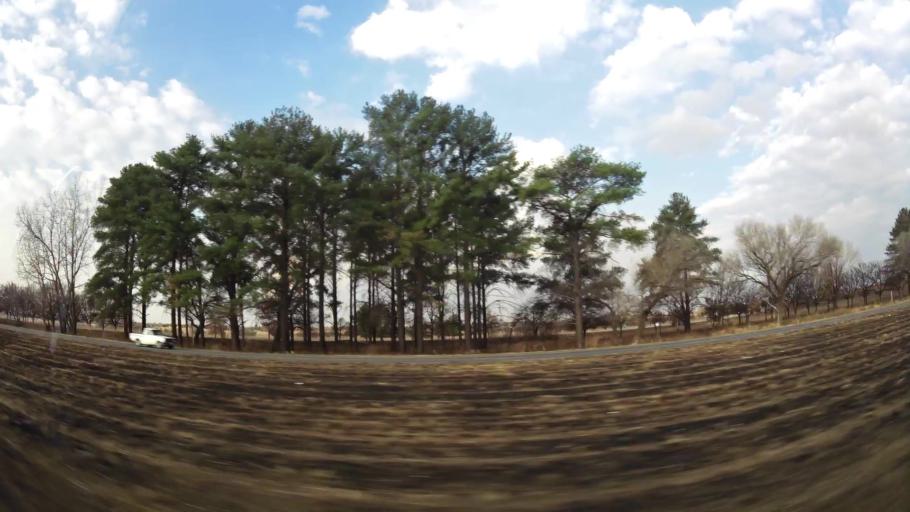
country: ZA
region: Orange Free State
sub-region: Fezile Dabi District Municipality
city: Sasolburg
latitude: -26.7814
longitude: 27.8242
